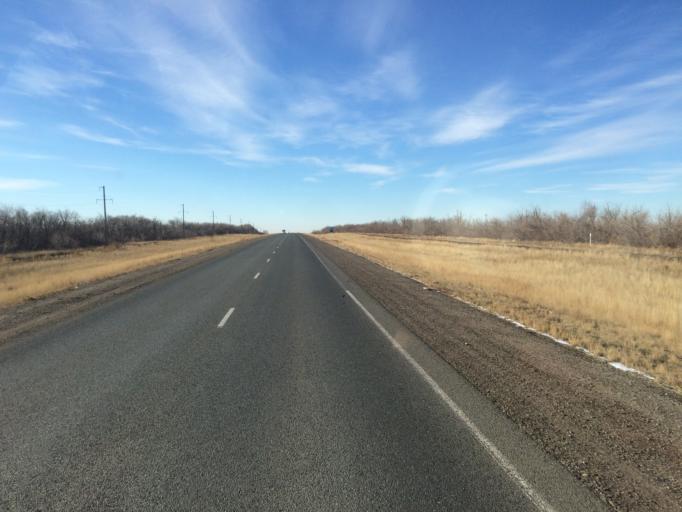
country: KZ
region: Aqtoebe
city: Aqtobe
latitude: 50.2473
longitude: 56.8018
